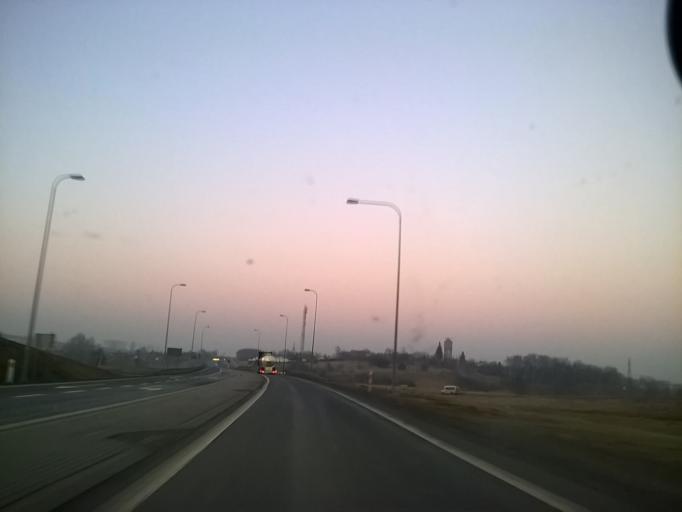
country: PL
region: Warmian-Masurian Voivodeship
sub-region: Powiat olsztynski
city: Barczewo
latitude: 53.8271
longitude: 20.6735
